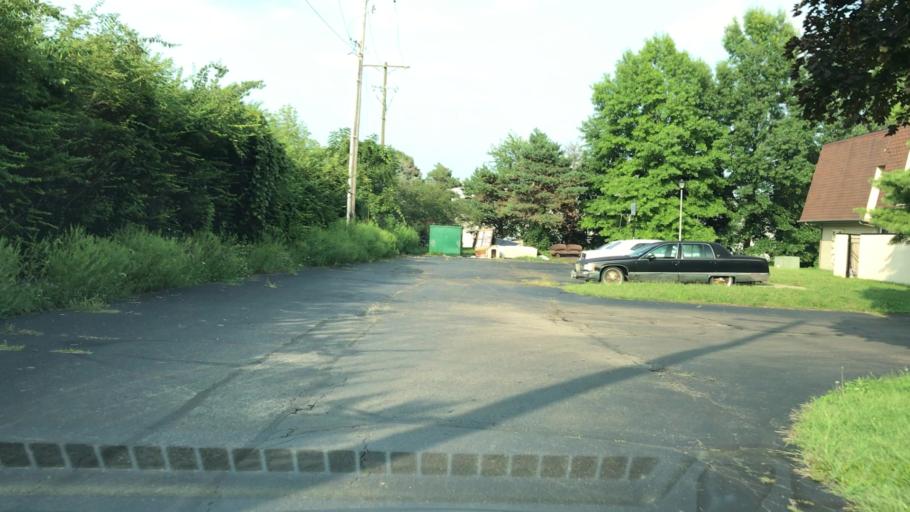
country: US
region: Ohio
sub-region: Franklin County
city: Lincoln Village
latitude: 39.9990
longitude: -83.1122
